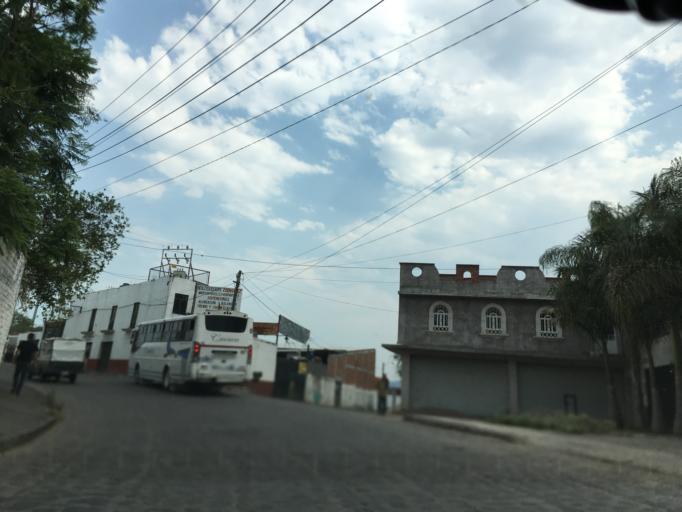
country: MX
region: Michoacan
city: Cuitzeo del Porvenir
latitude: 19.9648
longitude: -101.1413
